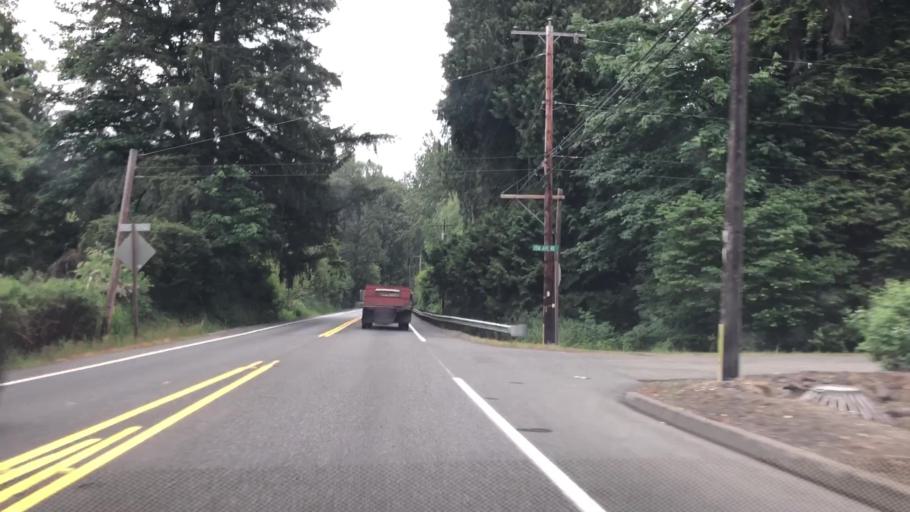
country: US
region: Washington
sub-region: King County
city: Cottage Lake
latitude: 47.7549
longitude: -122.0595
